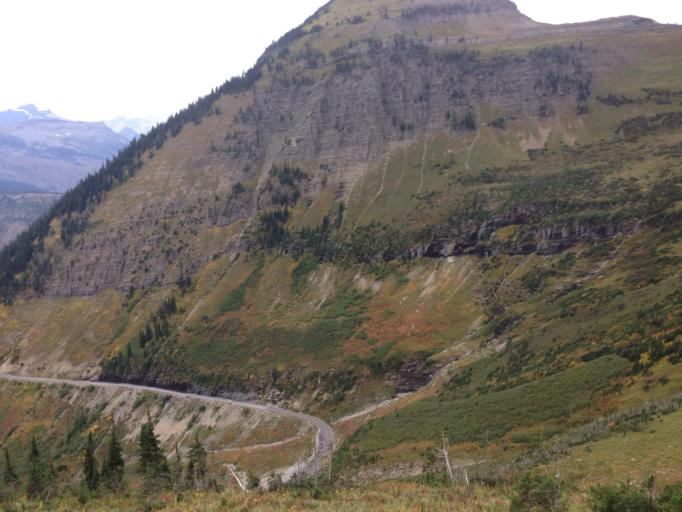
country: US
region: Montana
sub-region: Flathead County
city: Columbia Falls
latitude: 48.7254
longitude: -113.7194
